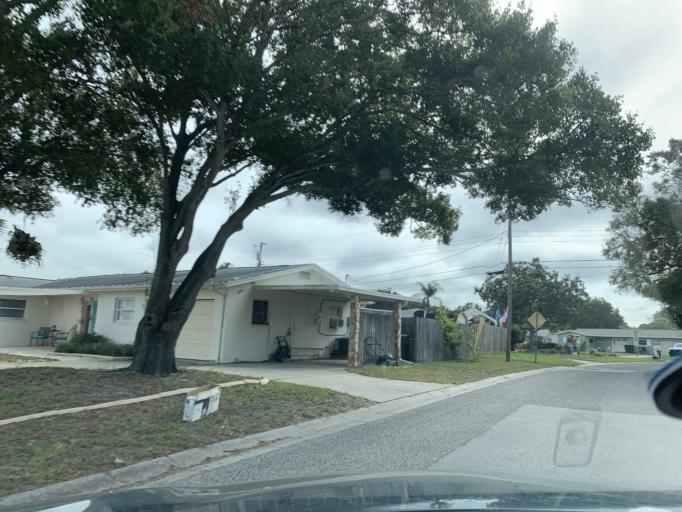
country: US
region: Florida
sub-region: Pinellas County
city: Ridgecrest
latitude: 27.8865
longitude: -82.7856
